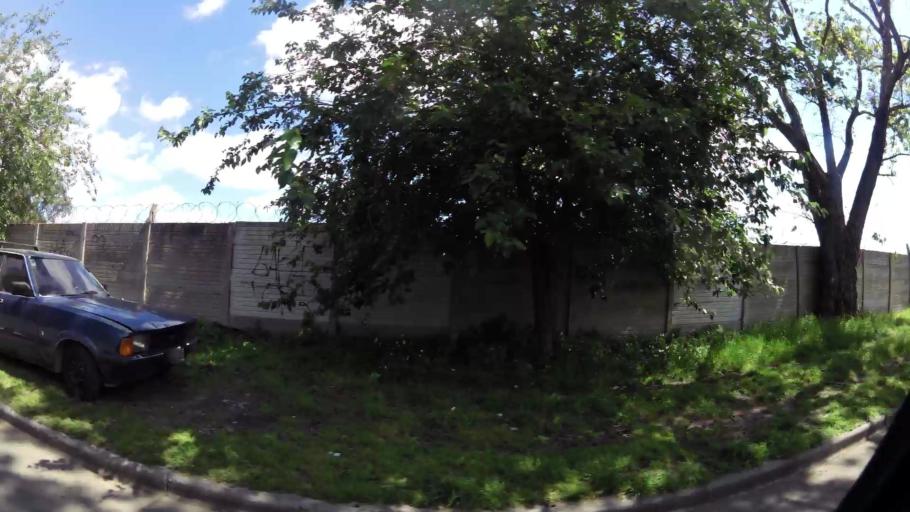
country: AR
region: Buenos Aires
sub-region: Partido de Lanus
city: Lanus
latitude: -34.6697
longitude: -58.4242
